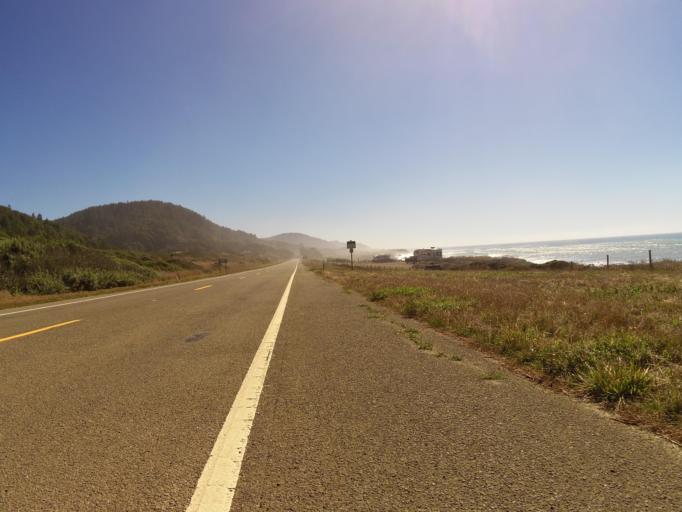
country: US
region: California
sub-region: Mendocino County
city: Fort Bragg
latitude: 39.6849
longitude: -123.7917
